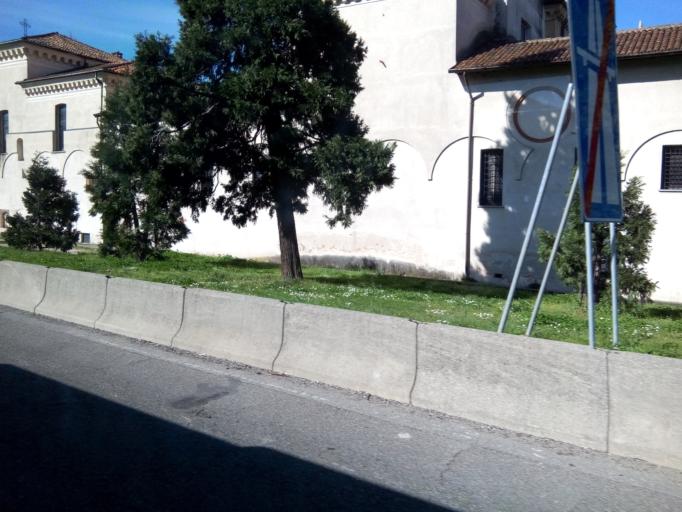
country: IT
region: Lombardy
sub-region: Citta metropolitana di Milano
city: Baranzate
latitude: 45.5026
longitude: 9.1302
